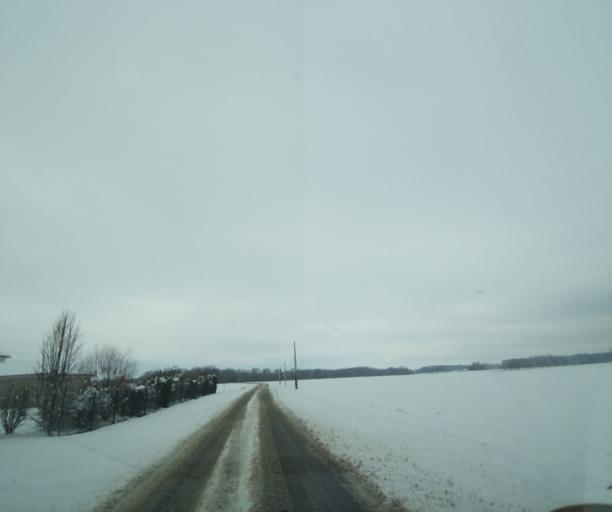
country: FR
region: Champagne-Ardenne
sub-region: Departement de la Haute-Marne
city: Montier-en-Der
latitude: 48.5307
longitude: 4.7467
